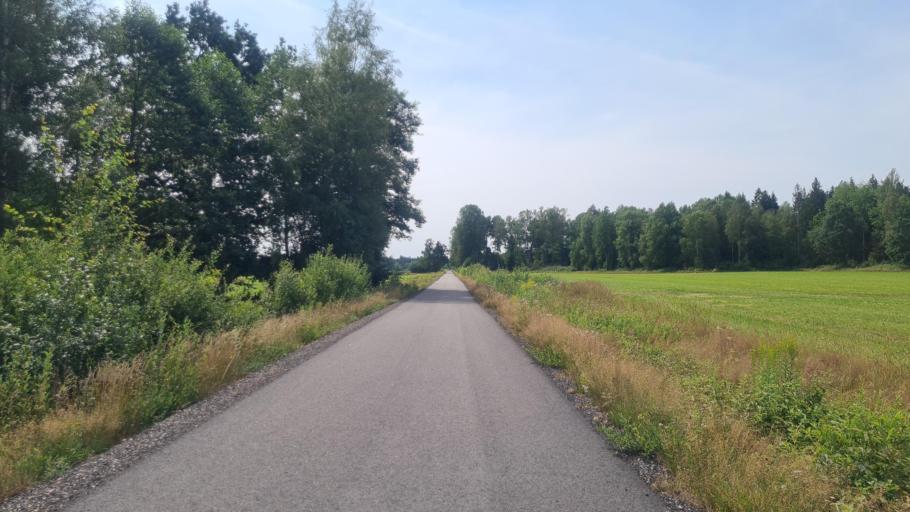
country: SE
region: Kronoberg
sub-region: Ljungby Kommun
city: Ljungby
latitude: 56.8580
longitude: 13.9756
